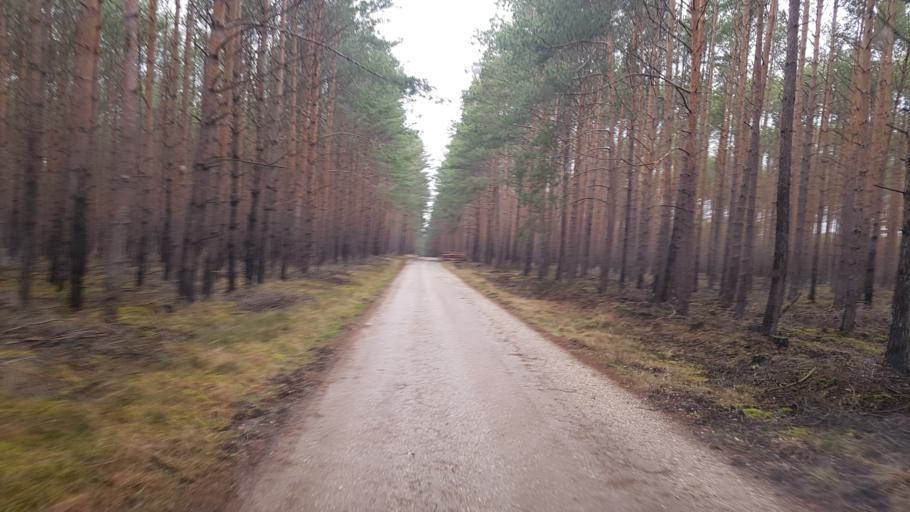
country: DE
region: Brandenburg
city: Sallgast
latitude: 51.6580
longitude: 13.8397
